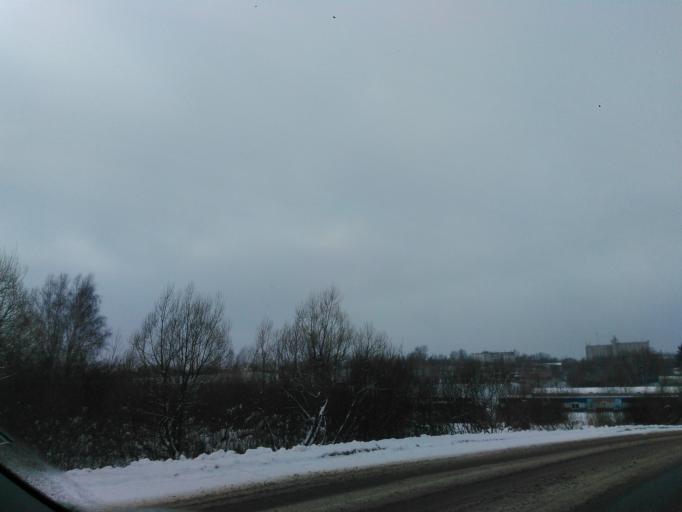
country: RU
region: Moskovskaya
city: Yakhroma
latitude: 56.2775
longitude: 37.4929
